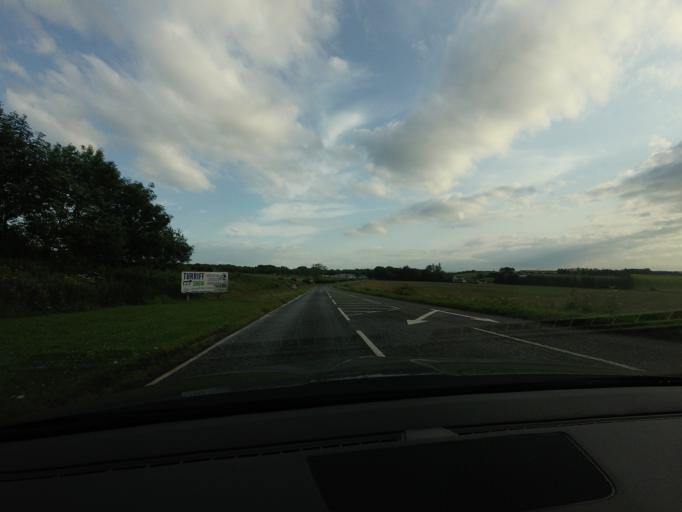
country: GB
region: Scotland
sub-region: Aberdeenshire
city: Turriff
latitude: 57.5482
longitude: -2.4429
